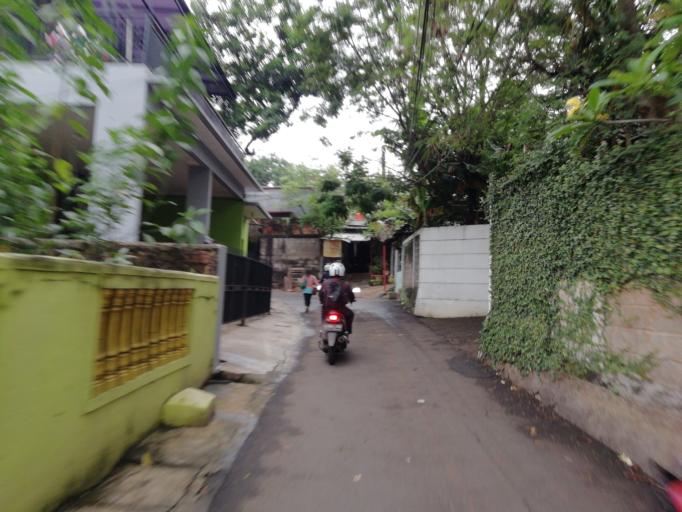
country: ID
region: Jakarta Raya
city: Jakarta
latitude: -6.3035
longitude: 106.8336
